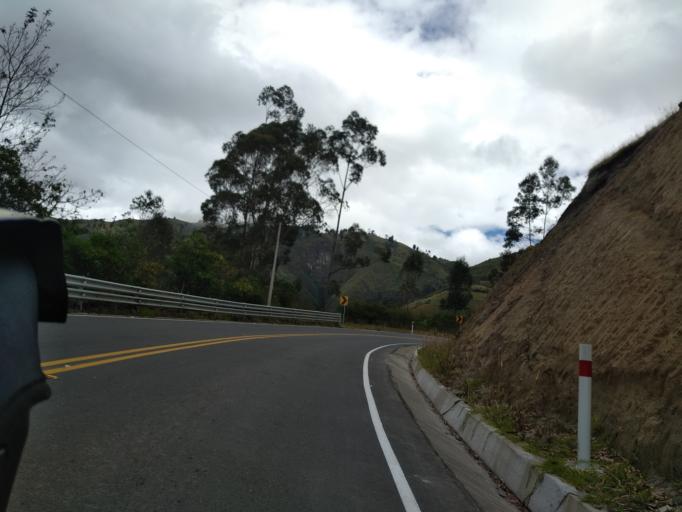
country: EC
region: Cotopaxi
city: Saquisili
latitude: -0.7533
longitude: -78.9046
